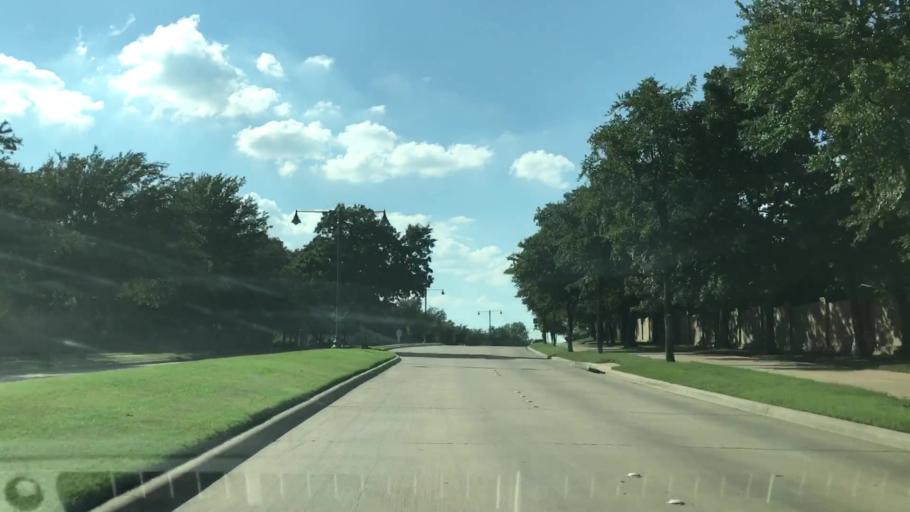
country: US
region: Texas
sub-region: Tarrant County
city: Keller
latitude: 32.9206
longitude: -97.2098
